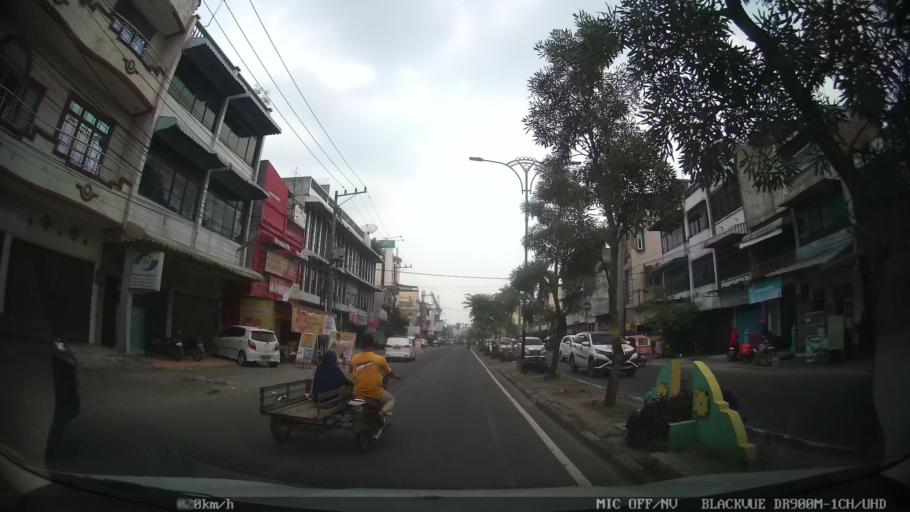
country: ID
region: North Sumatra
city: Medan
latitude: 3.5702
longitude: 98.6865
